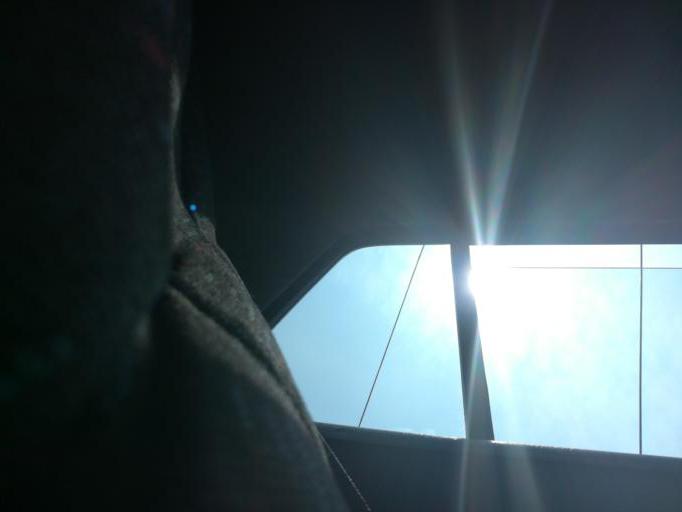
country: NG
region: Lagos
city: Lagos
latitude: 6.4552
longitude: 3.4009
